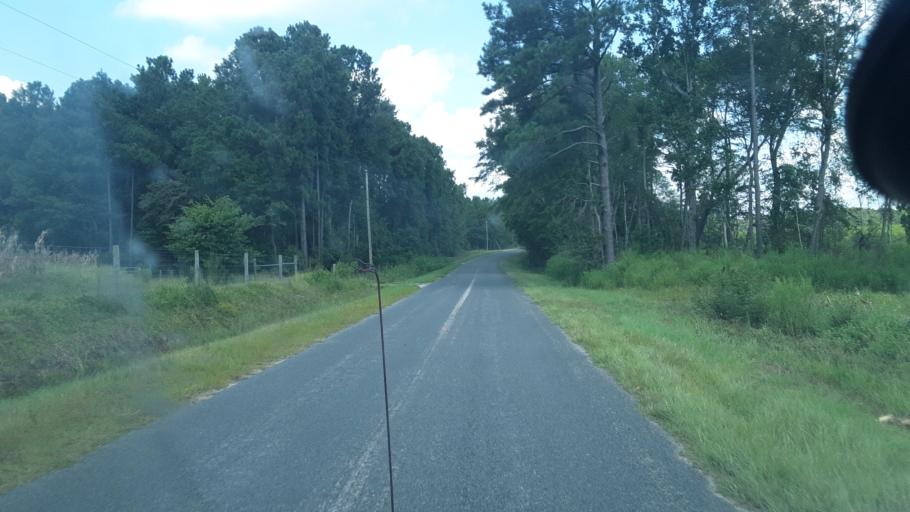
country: US
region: South Carolina
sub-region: Calhoun County
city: Oak Grove
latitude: 33.6789
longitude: -80.9707
